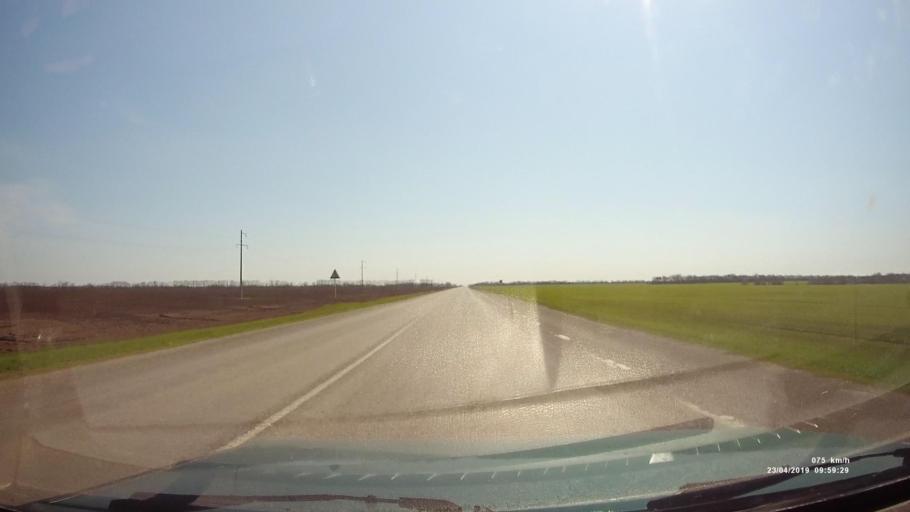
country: RU
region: Rostov
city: Sovetskoye
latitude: 46.7749
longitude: 42.1147
